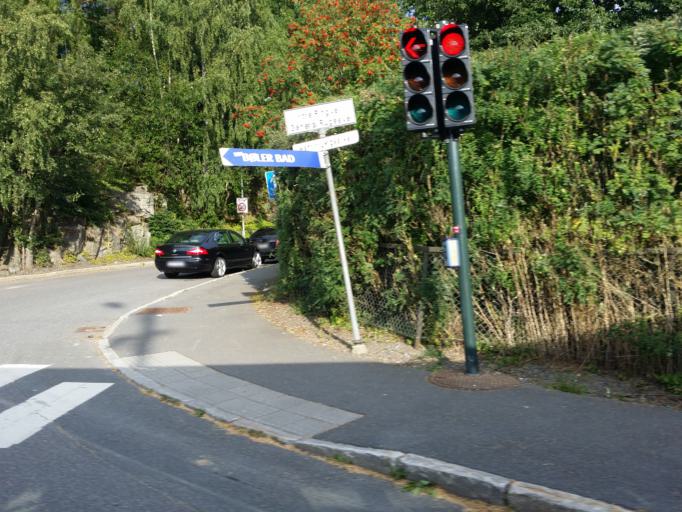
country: NO
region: Akershus
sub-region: Oppegard
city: Kolbotn
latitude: 59.8807
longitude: 10.8401
